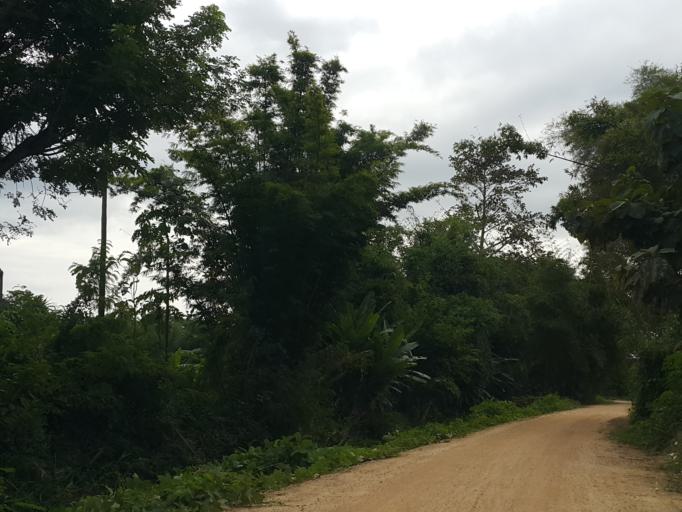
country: TH
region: Lampang
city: Hang Chat
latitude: 18.4720
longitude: 99.4169
